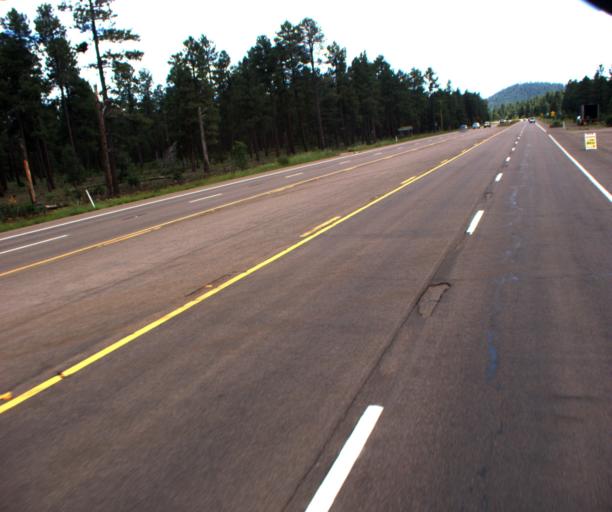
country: US
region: Arizona
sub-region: Navajo County
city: Pinetop-Lakeside
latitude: 34.0904
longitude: -109.9075
